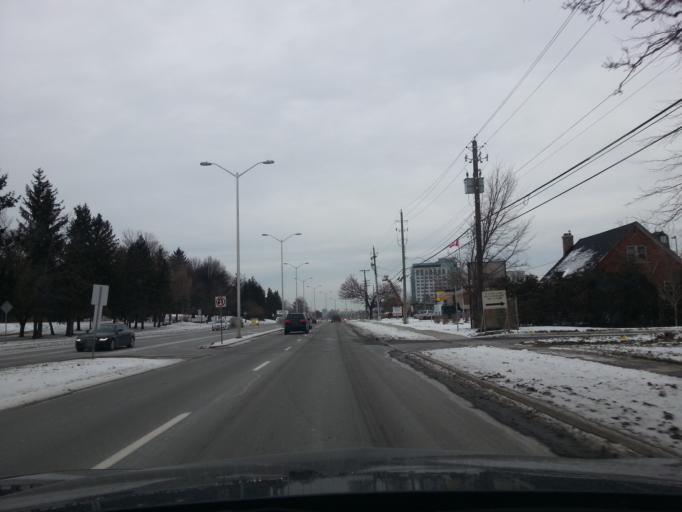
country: CA
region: Ontario
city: Ottawa
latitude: 45.3704
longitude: -75.6903
